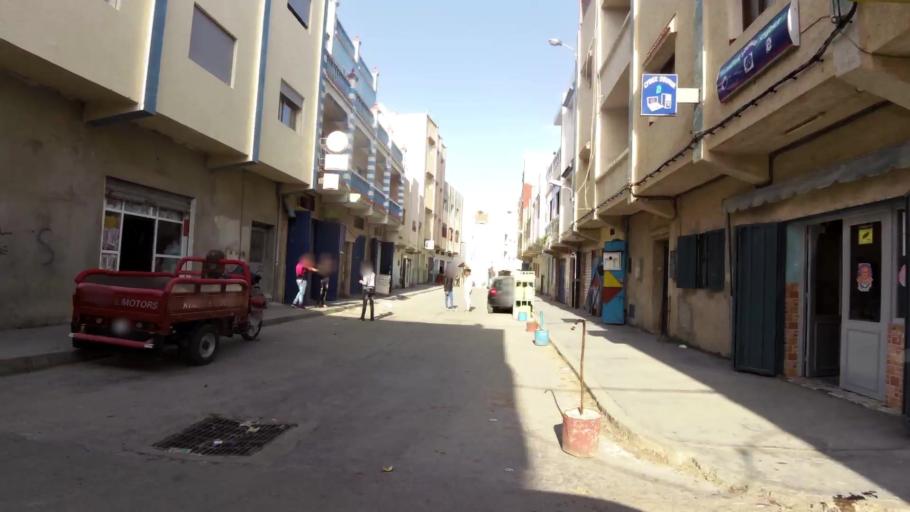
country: MA
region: Tanger-Tetouan
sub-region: Tetouan
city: Martil
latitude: 35.6127
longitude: -5.2732
